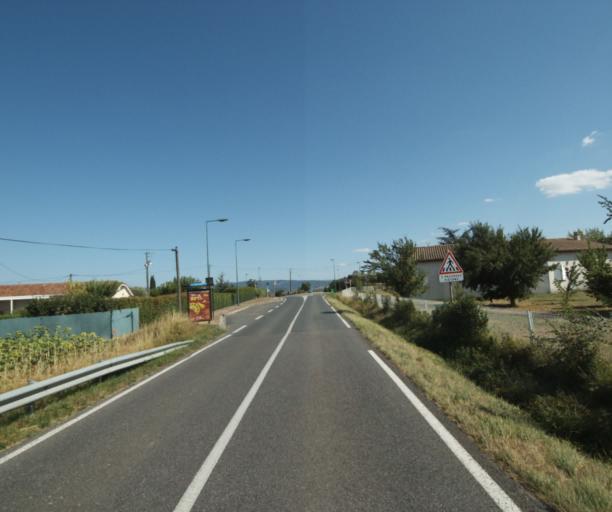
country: FR
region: Midi-Pyrenees
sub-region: Departement de la Haute-Garonne
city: Saint-Felix-Lauragais
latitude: 43.4817
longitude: 1.9155
